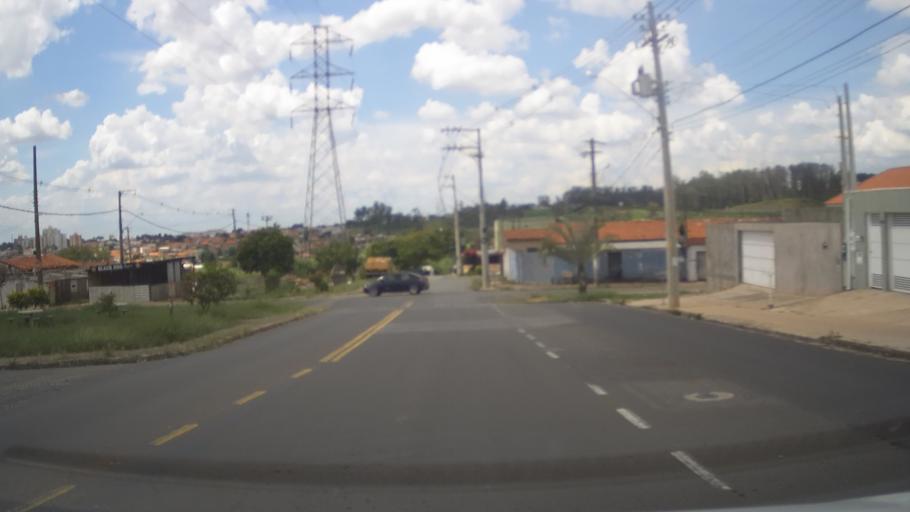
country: BR
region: Sao Paulo
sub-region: Campinas
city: Campinas
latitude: -22.9227
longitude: -47.0274
